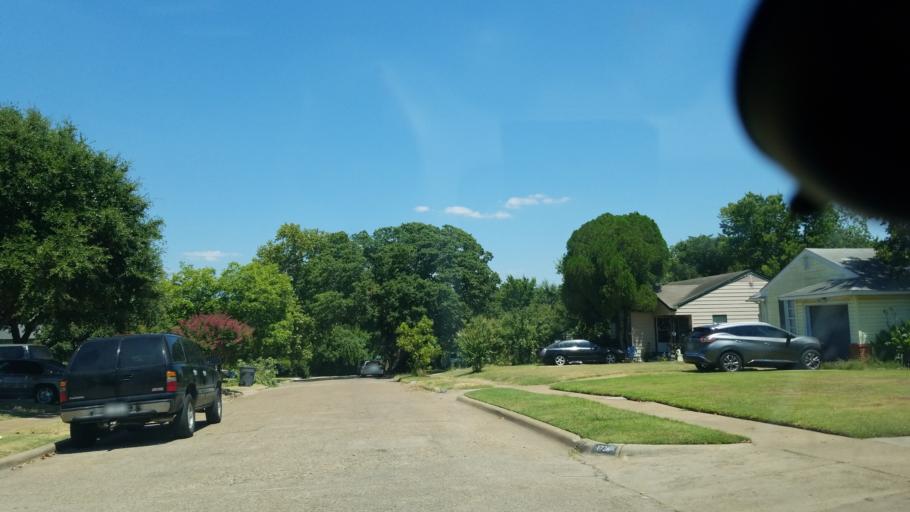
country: US
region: Texas
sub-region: Dallas County
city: Cockrell Hill
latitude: 32.7262
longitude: -96.8496
